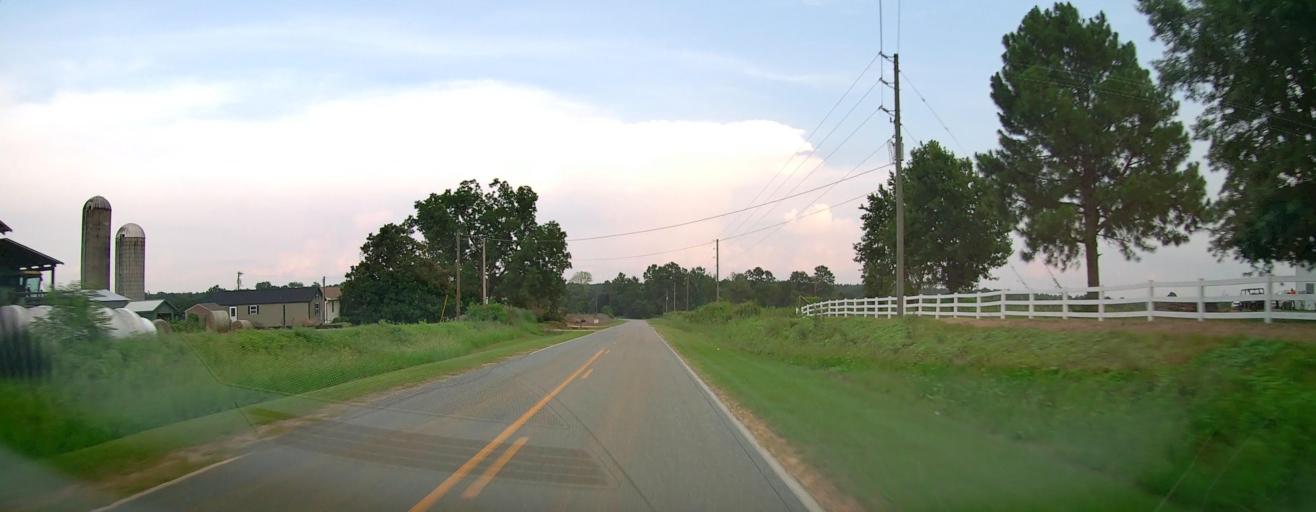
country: US
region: Georgia
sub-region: Laurens County
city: East Dublin
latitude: 32.6425
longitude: -82.8146
